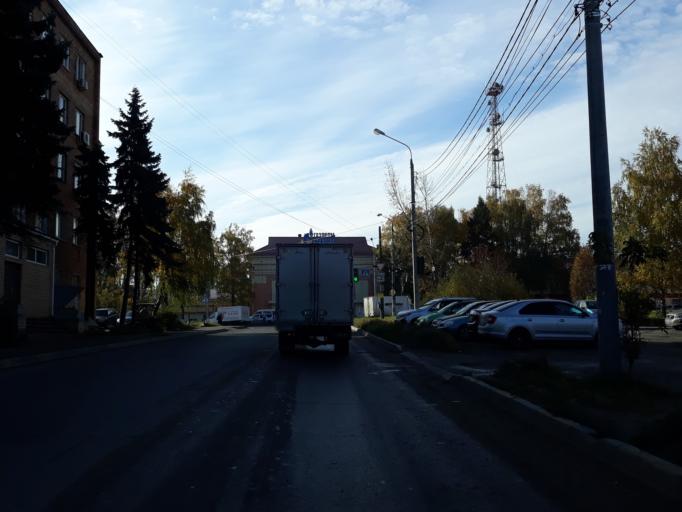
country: RU
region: Nizjnij Novgorod
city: Nizhniy Novgorod
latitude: 56.2419
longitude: 43.9840
